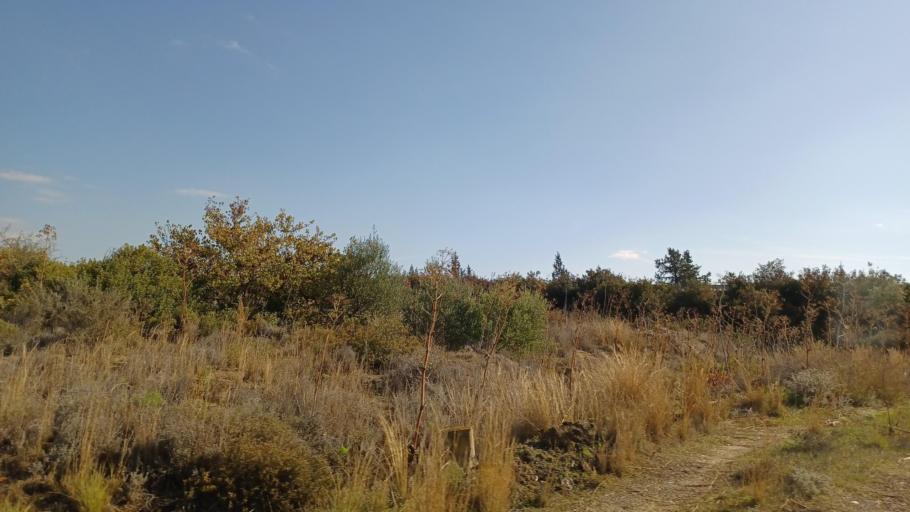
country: CY
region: Larnaka
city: Kofinou
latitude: 34.7565
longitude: 33.3183
